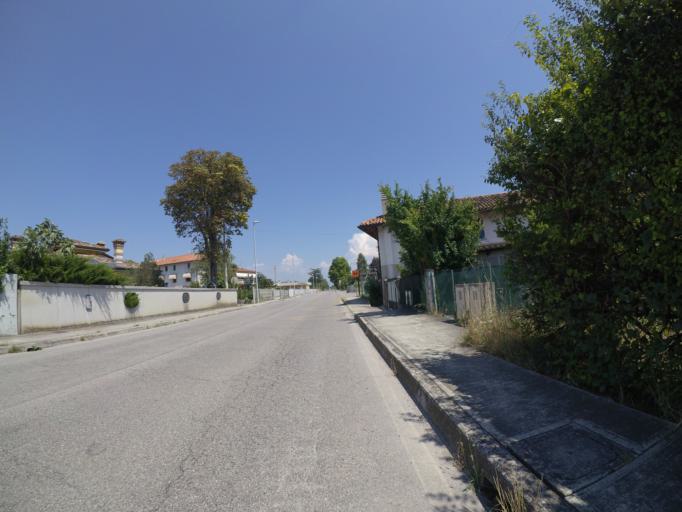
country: IT
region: Friuli Venezia Giulia
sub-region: Provincia di Udine
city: Talmassons
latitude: 45.9250
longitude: 13.1492
